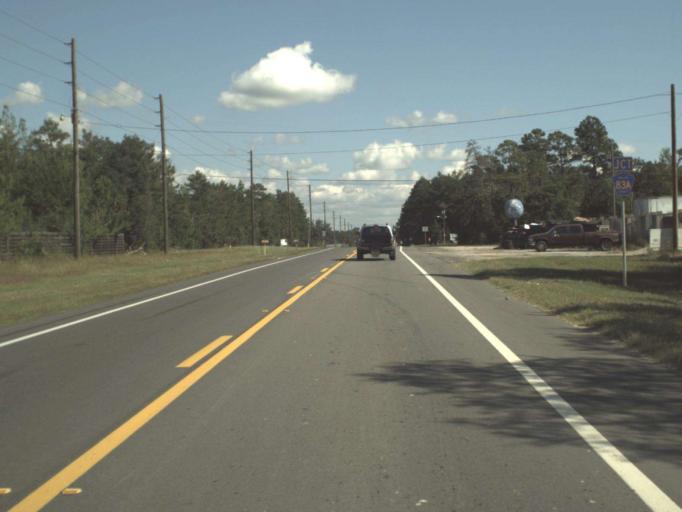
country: US
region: Florida
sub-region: Walton County
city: Freeport
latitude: 30.5101
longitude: -86.1714
